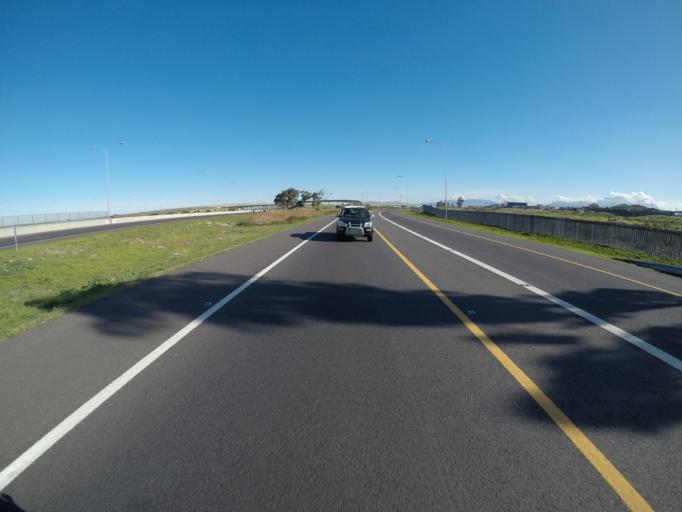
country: ZA
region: Western Cape
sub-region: City of Cape Town
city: Lansdowne
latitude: -33.9966
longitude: 18.6373
